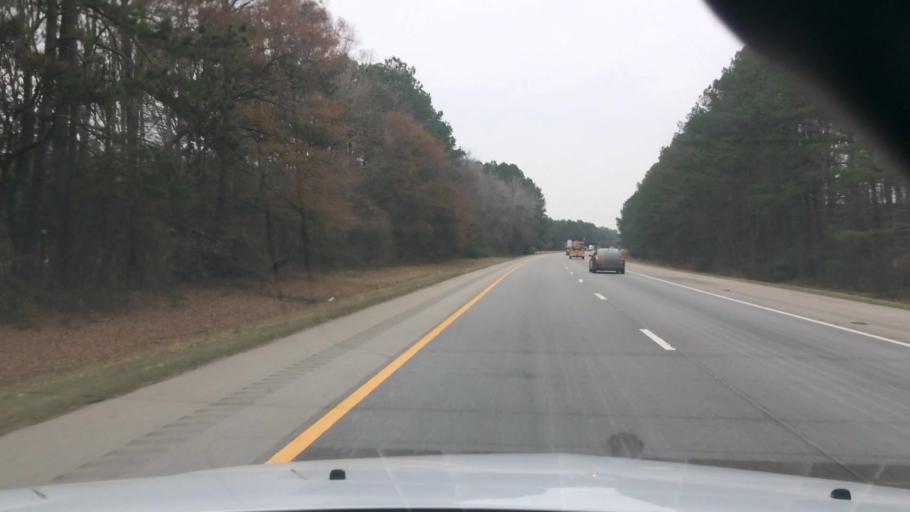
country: US
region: North Carolina
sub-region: Wilson County
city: Wilson
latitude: 35.7795
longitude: -78.0017
